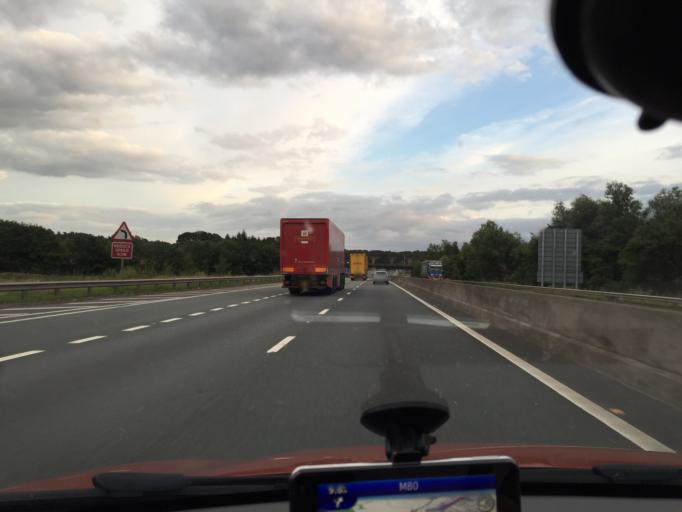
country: GB
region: Scotland
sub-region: Falkirk
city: Dunipace
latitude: 55.9869
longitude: -3.9439
